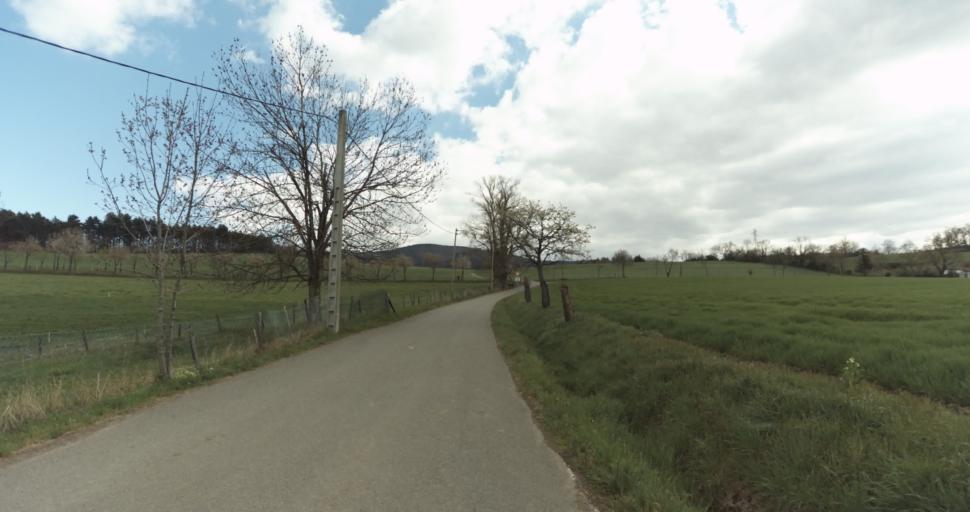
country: FR
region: Rhone-Alpes
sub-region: Departement de la Loire
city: Saint-Jean-Bonnefonds
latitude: 45.4480
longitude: 4.4551
